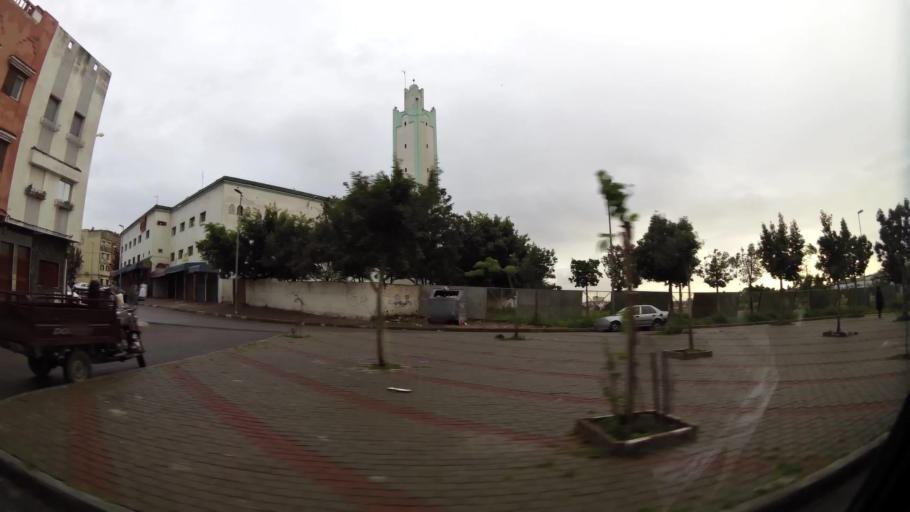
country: MA
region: Grand Casablanca
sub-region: Casablanca
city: Casablanca
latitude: 33.5547
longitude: -7.5807
